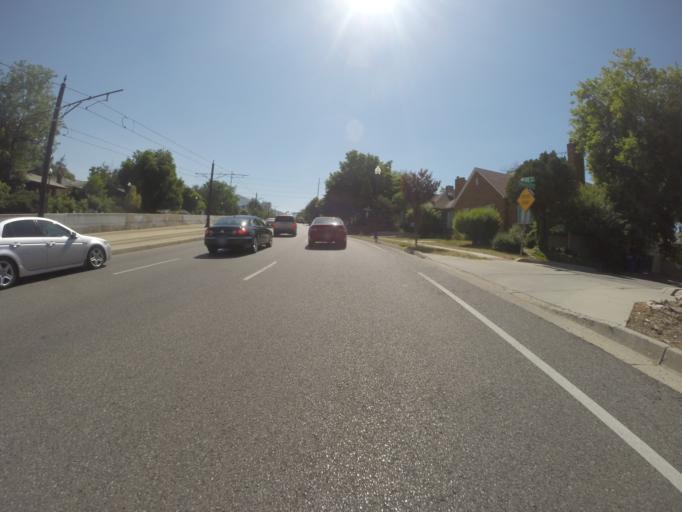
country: US
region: Utah
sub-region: Salt Lake County
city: Salt Lake City
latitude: 40.7584
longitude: -111.8616
